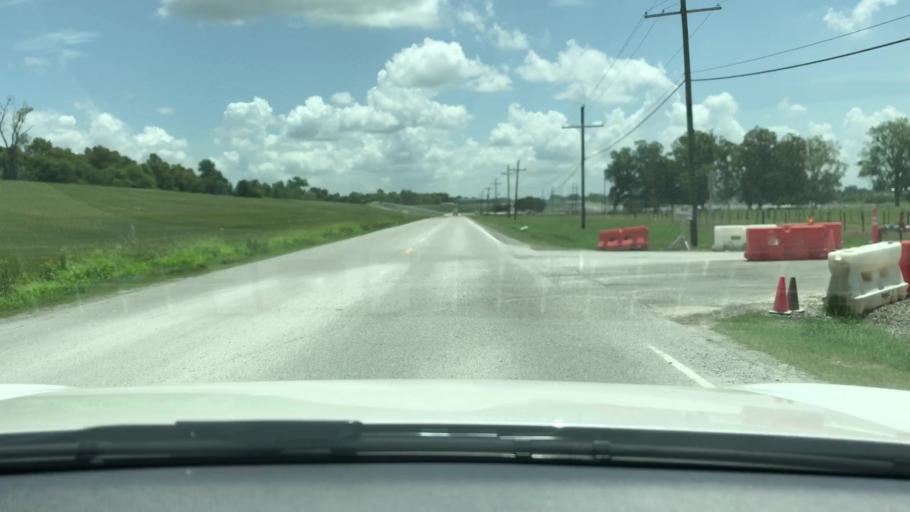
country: US
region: Louisiana
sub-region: Iberville Parish
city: Plaquemine
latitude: 30.2733
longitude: -91.1779
